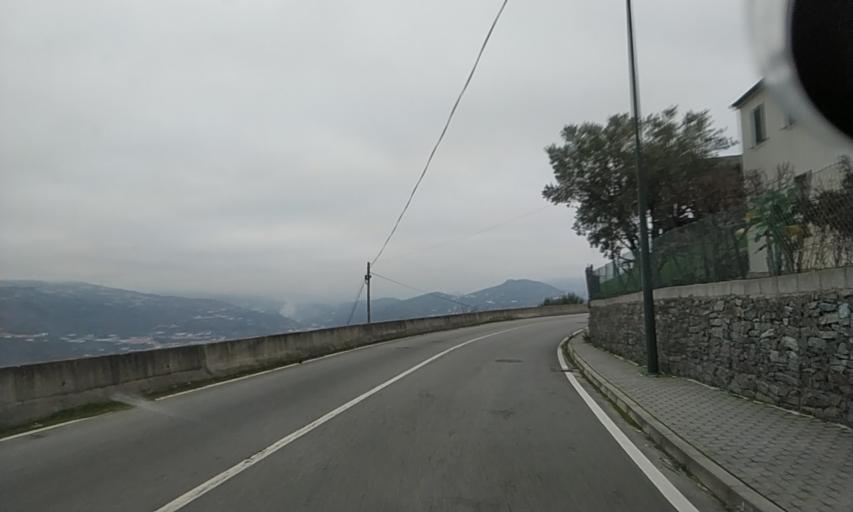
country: PT
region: Vila Real
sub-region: Peso da Regua
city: Peso da Regua
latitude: 41.1316
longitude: -7.7996
